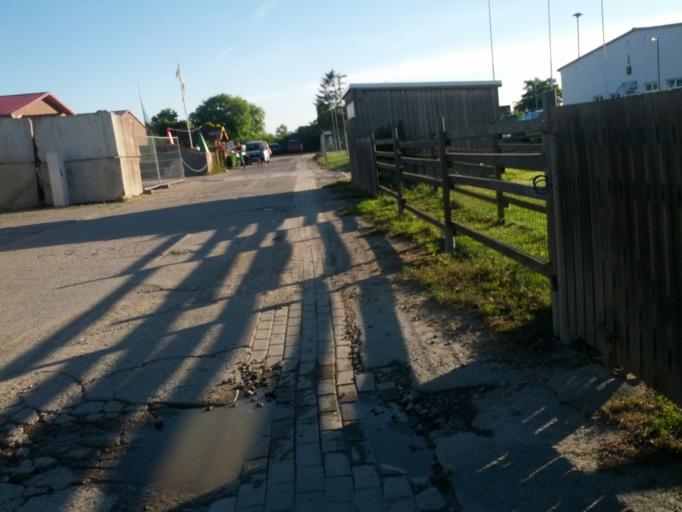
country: DE
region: Mecklenburg-Vorpommern
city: Bastorf
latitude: 54.1116
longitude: 11.6308
